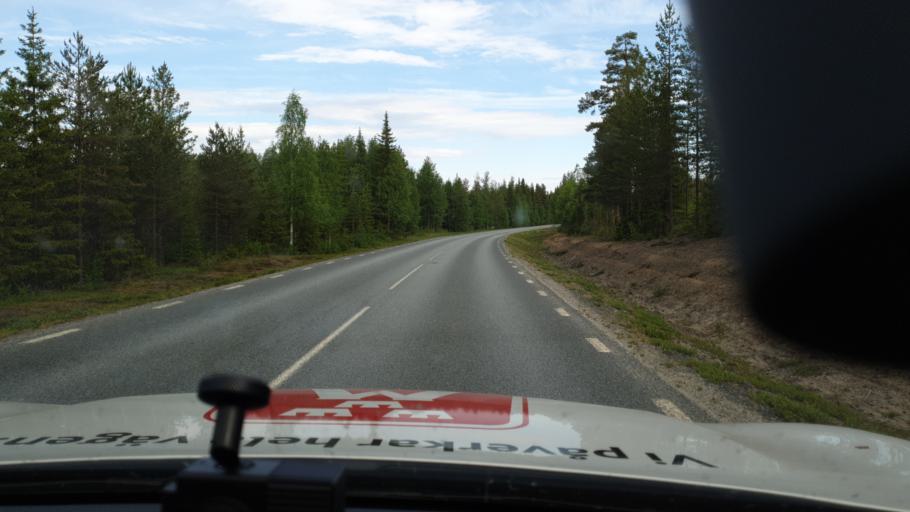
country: SE
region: Vaesterbotten
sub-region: Lycksele Kommun
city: Soderfors
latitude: 65.1290
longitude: 18.2751
